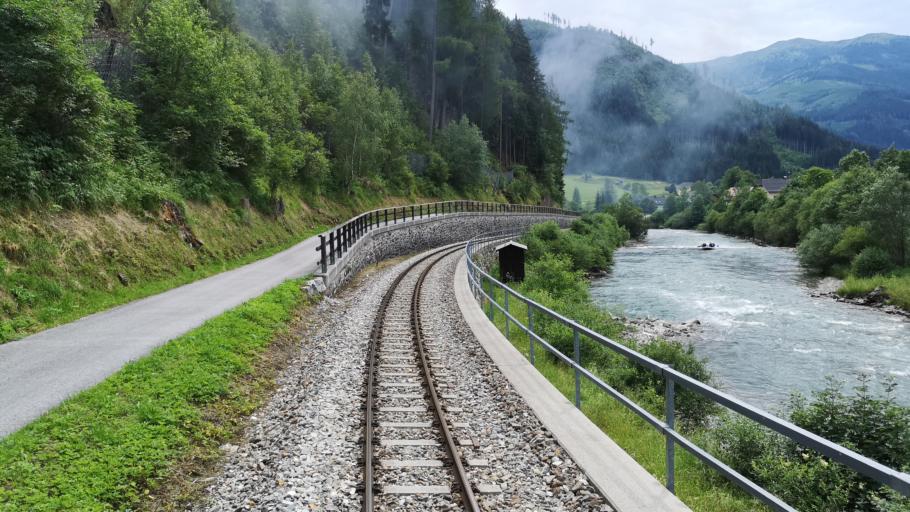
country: AT
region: Salzburg
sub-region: Politischer Bezirk Tamsweg
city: Ramingstein
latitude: 47.0806
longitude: 13.8148
